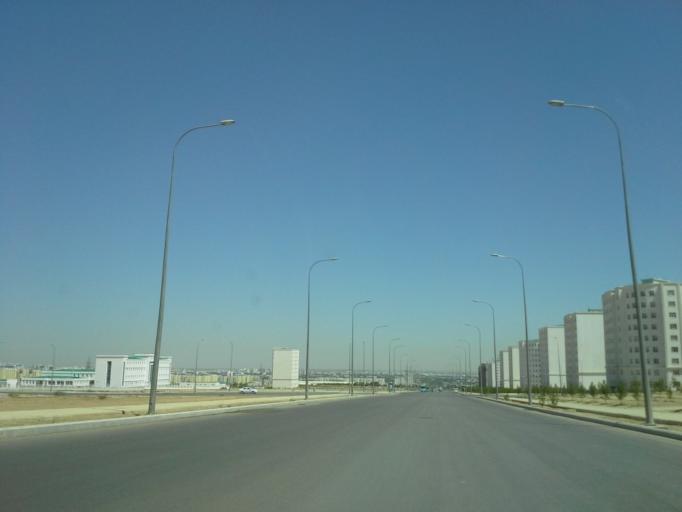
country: TM
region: Ahal
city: Ashgabat
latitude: 37.8888
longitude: 58.4056
